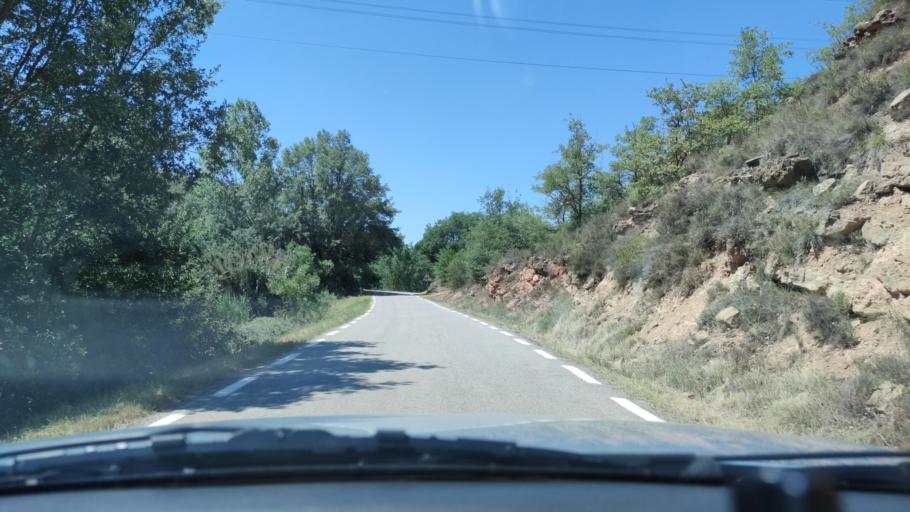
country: ES
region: Catalonia
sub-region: Provincia de Lleida
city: Tora de Riubregos
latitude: 41.8229
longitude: 1.4198
